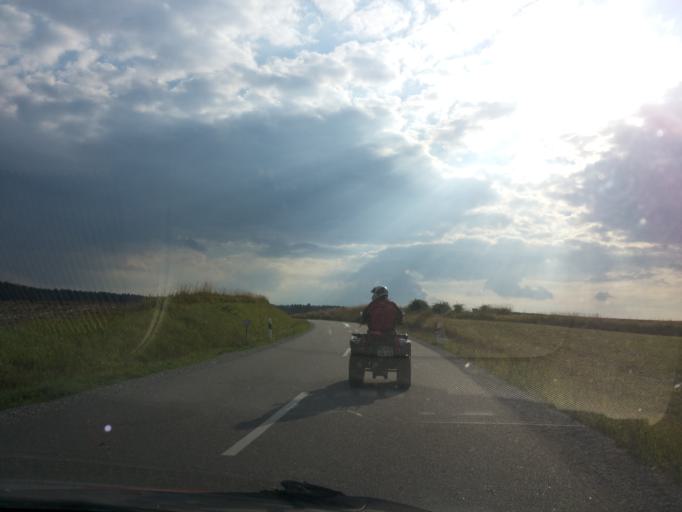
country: DE
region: Bavaria
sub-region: Upper Palatinate
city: Dietfurt
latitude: 48.9708
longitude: 11.5560
